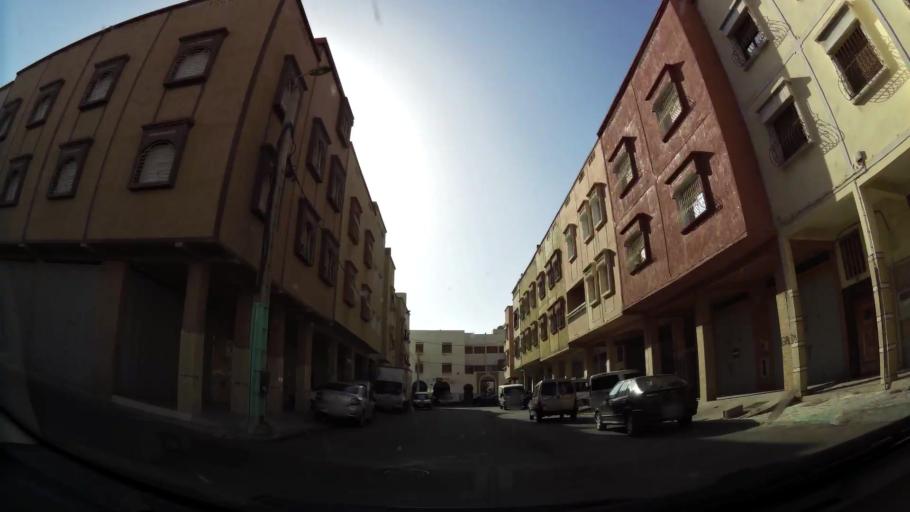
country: MA
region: Souss-Massa-Draa
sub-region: Inezgane-Ait Mellou
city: Inezgane
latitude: 30.3710
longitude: -9.5305
